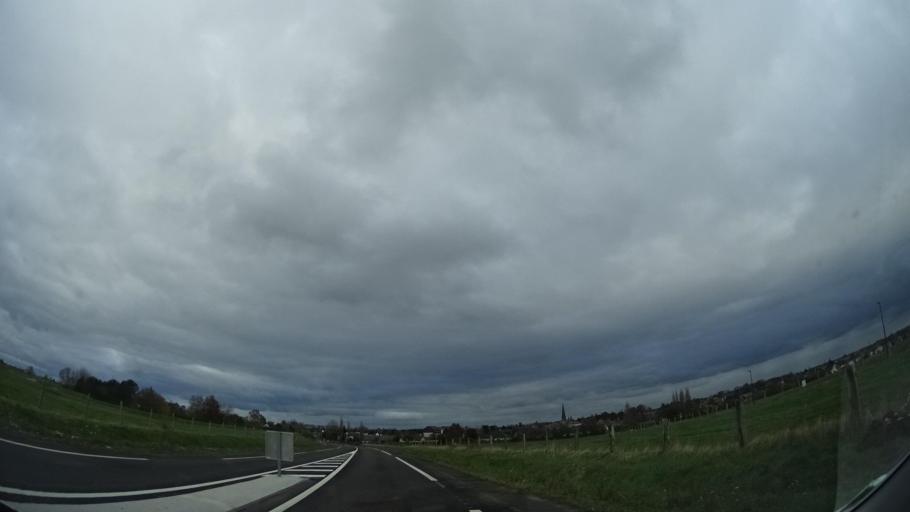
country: FR
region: Haute-Normandie
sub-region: Departement de la Seine-Maritime
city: Octeville-sur-Mer
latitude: 49.5504
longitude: 0.1112
